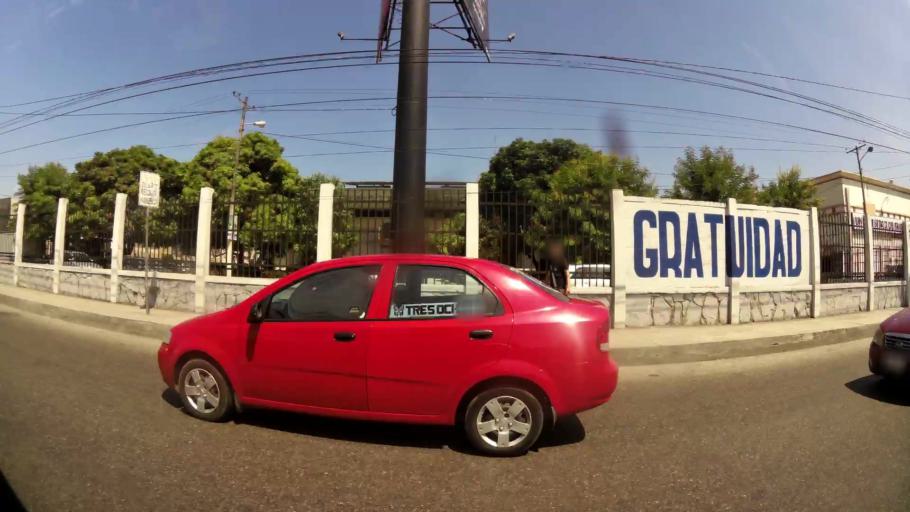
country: EC
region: Guayas
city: Guayaquil
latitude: -2.1815
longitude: -79.8963
